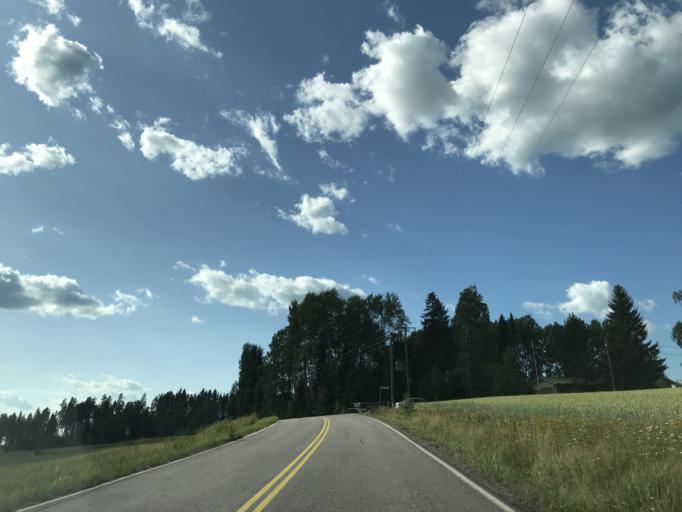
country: FI
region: Uusimaa
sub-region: Helsinki
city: Nurmijaervi
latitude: 60.4493
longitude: 24.6539
